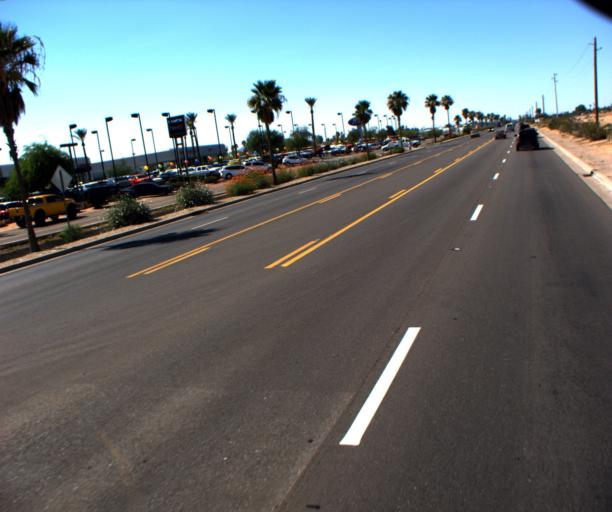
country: US
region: Arizona
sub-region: Pinal County
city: Casa Grande
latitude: 32.9074
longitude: -111.7574
